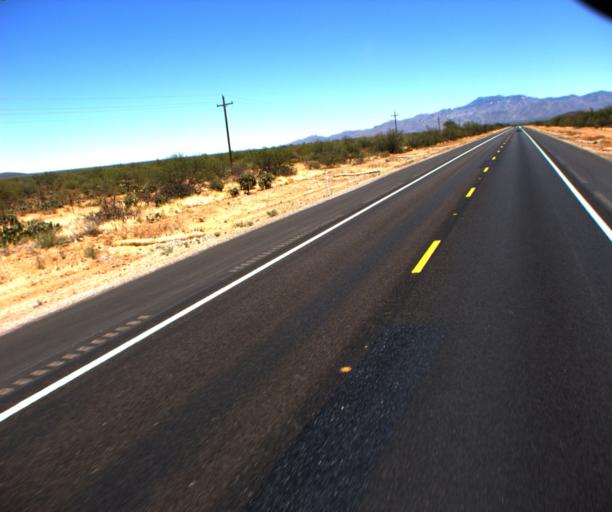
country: US
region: Arizona
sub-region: Pima County
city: Sells
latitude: 31.9177
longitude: -111.8437
